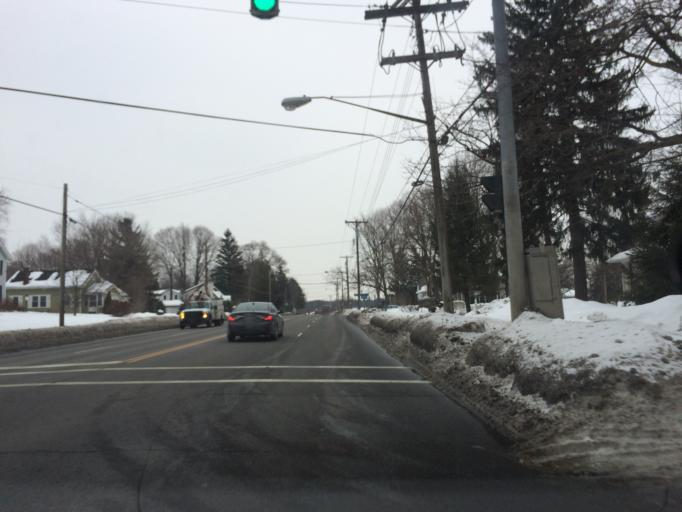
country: US
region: New York
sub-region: Monroe County
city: East Rochester
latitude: 43.1050
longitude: -77.4895
